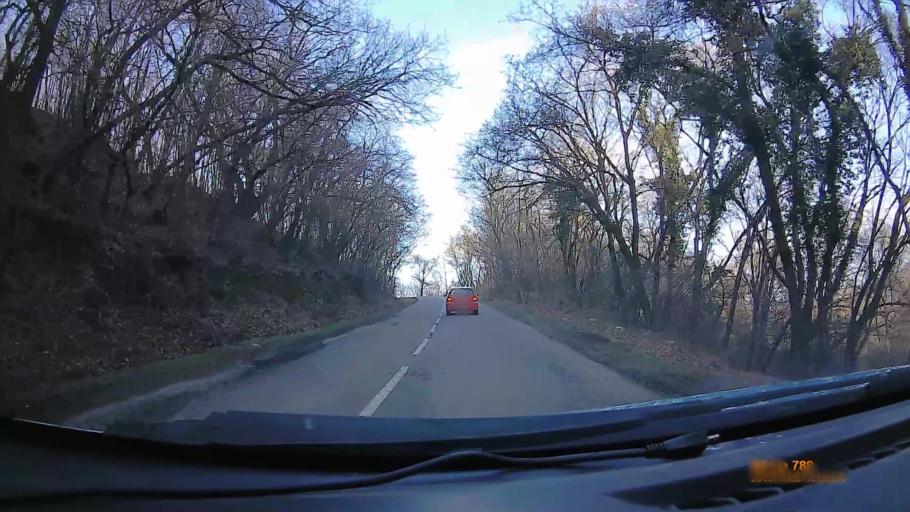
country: HU
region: Heves
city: Sirok
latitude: 47.8937
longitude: 20.1882
